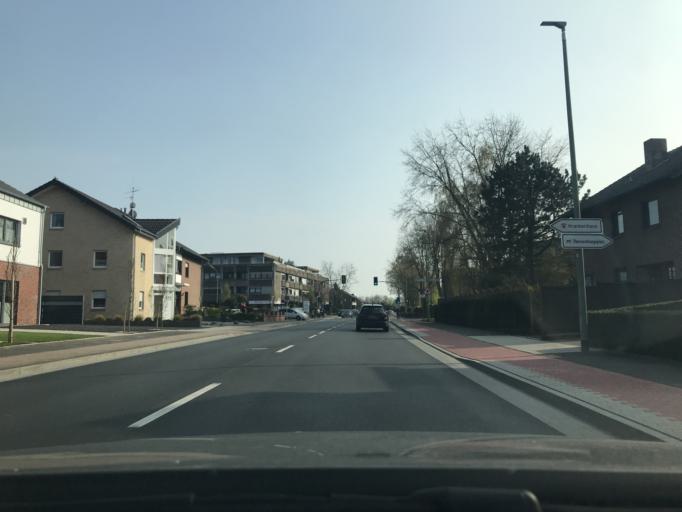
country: DE
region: North Rhine-Westphalia
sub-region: Regierungsbezirk Dusseldorf
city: Goch
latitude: 51.6753
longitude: 6.1722
